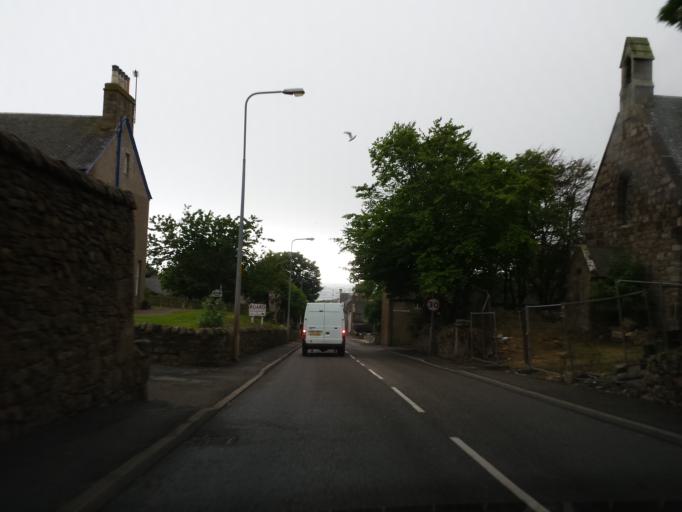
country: GB
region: Scotland
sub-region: Highland
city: Brora
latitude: 58.1176
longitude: -3.6489
